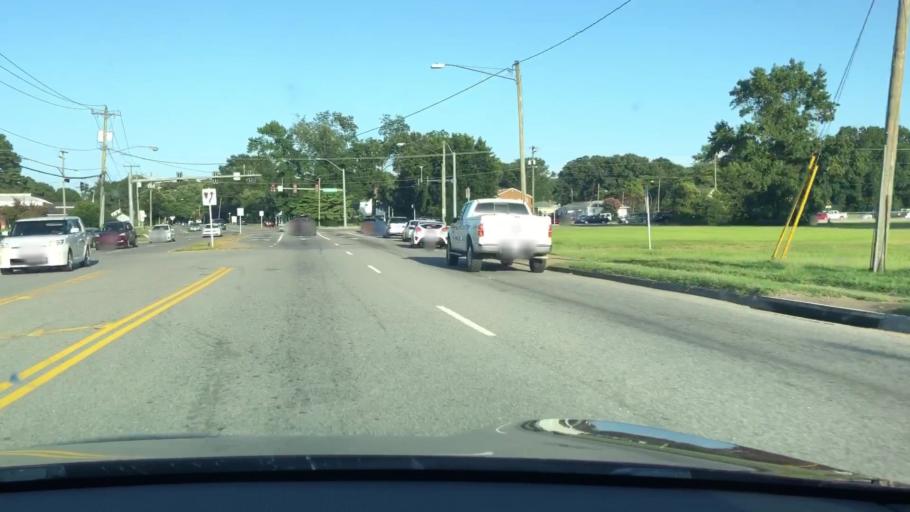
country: US
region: Virginia
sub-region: City of Virginia Beach
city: Virginia Beach
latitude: 36.8426
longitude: -76.0224
